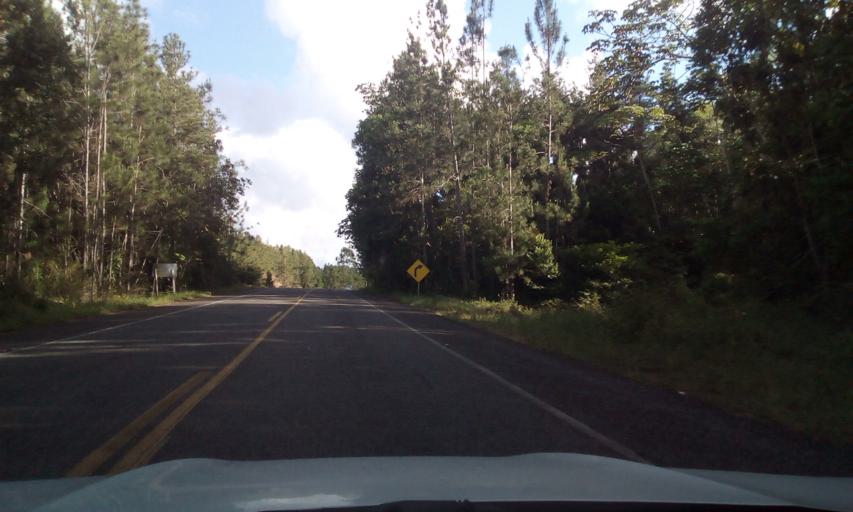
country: BR
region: Bahia
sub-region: Conde
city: Conde
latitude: -12.1059
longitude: -37.7835
